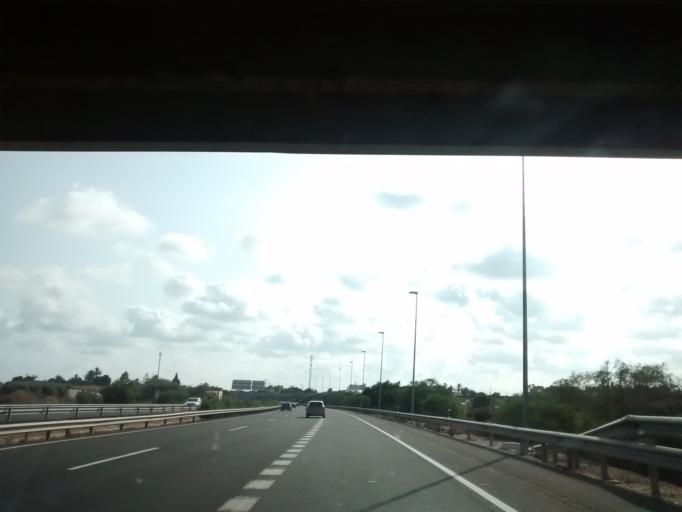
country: ES
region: Valencia
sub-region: Provincia de Alicante
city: el Campello
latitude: 38.4350
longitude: -0.4084
